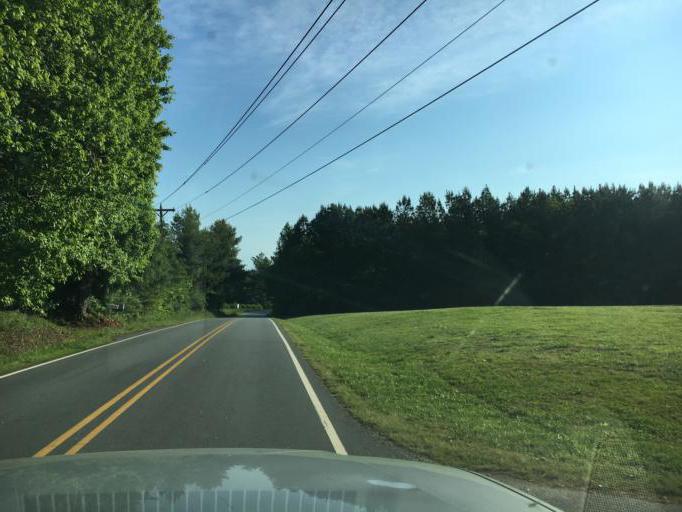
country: US
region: North Carolina
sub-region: Rutherford County
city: Rutherfordton
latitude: 35.3656
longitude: -81.9776
